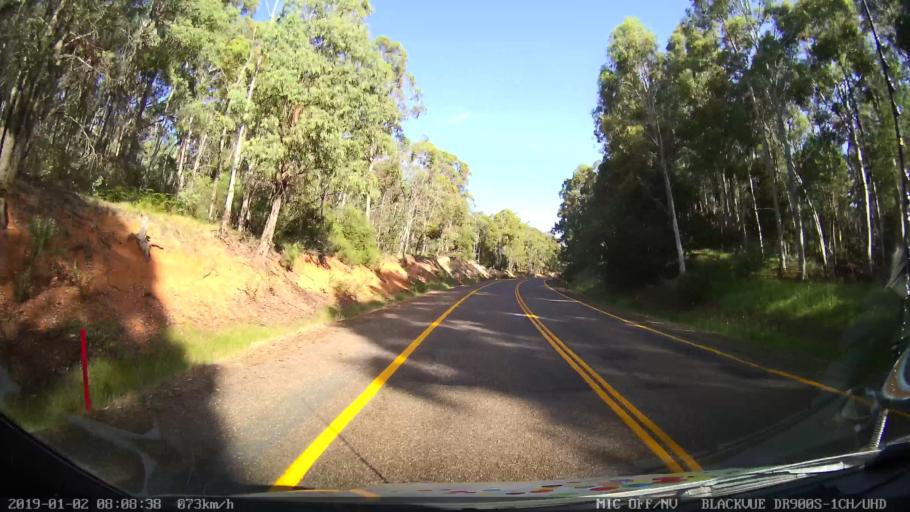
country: AU
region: New South Wales
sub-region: Tumut Shire
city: Tumut
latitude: -35.6150
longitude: 148.3834
